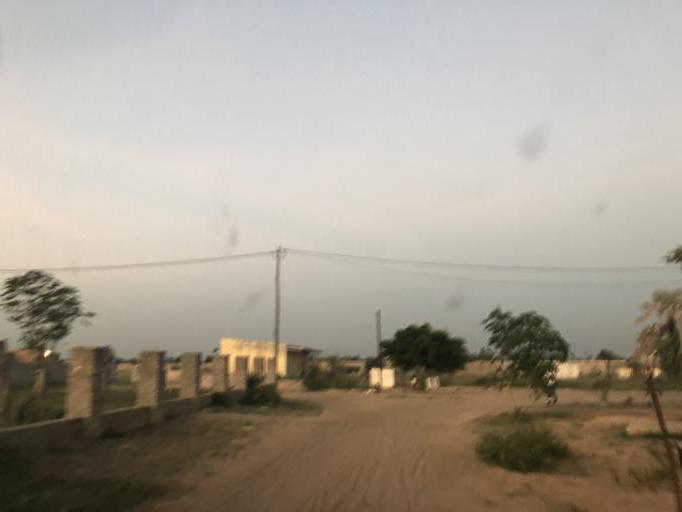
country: AO
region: Cunene
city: Ondjiva
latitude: -17.0622
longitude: 15.7060
